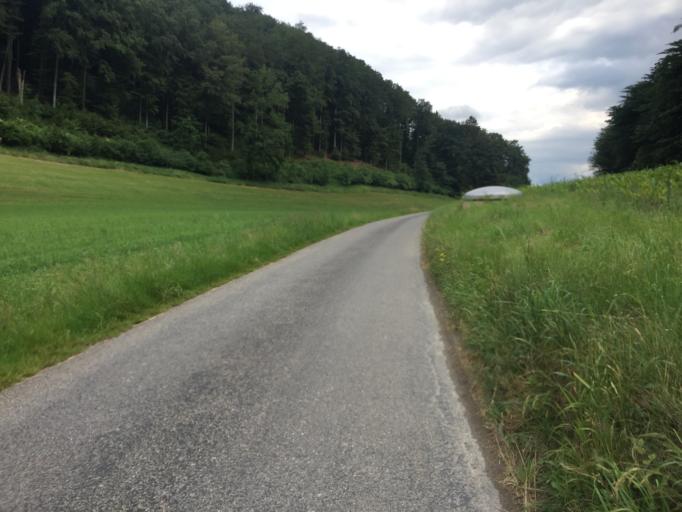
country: CH
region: Bern
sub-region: Bern-Mittelland District
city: Stettlen
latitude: 46.9461
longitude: 7.5095
